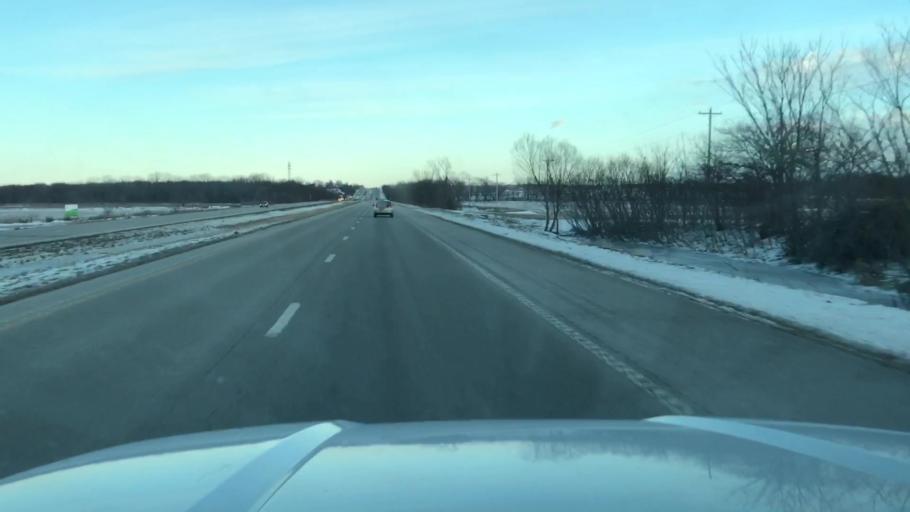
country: US
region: Missouri
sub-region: Clinton County
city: Gower
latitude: 39.7474
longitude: -94.6704
